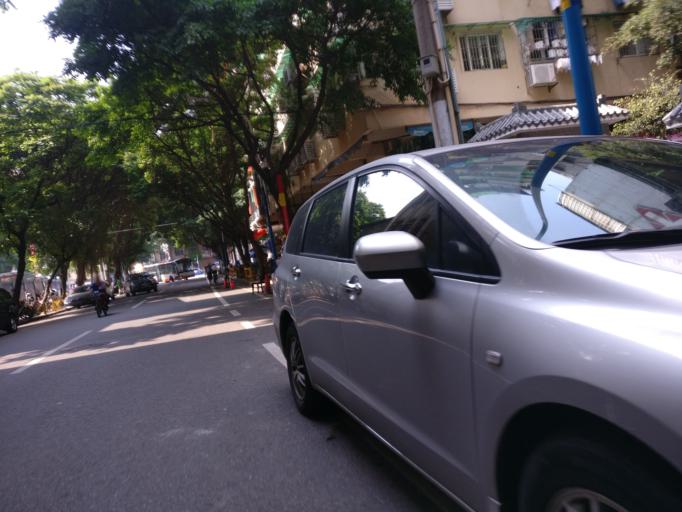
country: CN
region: Guangdong
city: Guangzhou
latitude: 23.1282
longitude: 113.2698
